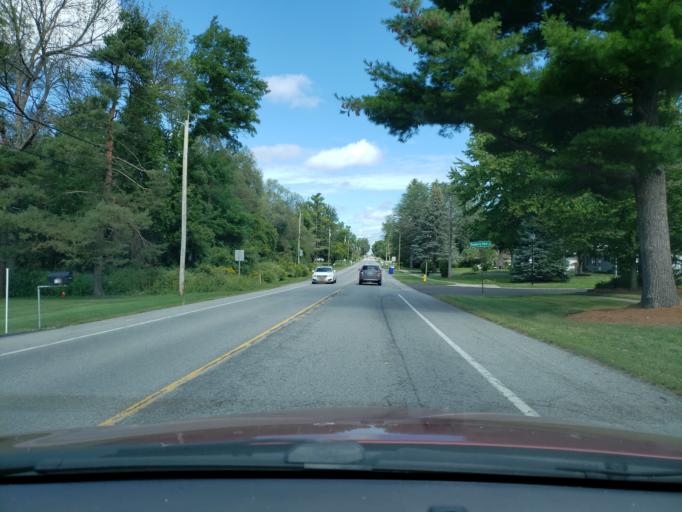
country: US
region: New York
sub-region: Monroe County
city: Greece
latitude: 43.2465
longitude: -77.7331
